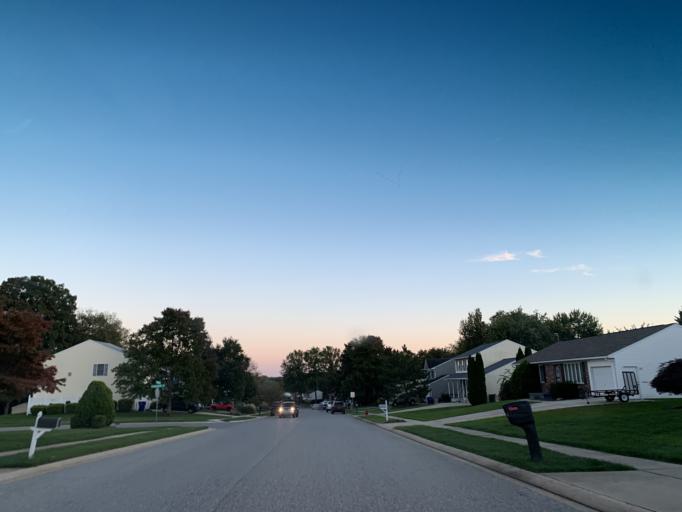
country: US
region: Maryland
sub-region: Harford County
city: South Bel Air
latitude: 39.5441
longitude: -76.3025
